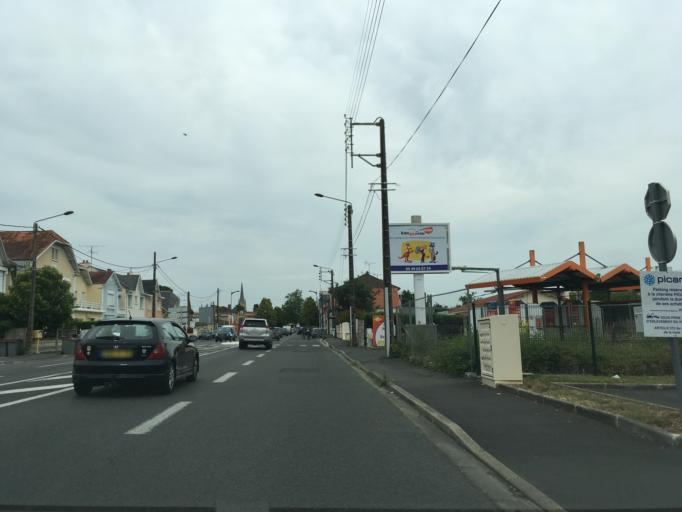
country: FR
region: Poitou-Charentes
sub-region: Departement des Deux-Sevres
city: Niort
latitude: 46.3154
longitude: -0.4740
